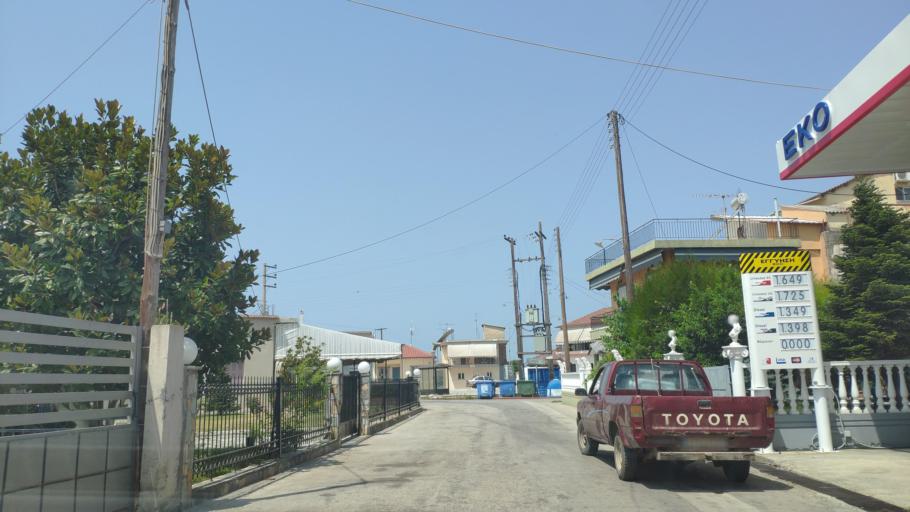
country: GR
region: Epirus
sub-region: Nomos Artas
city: Neochori
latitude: 39.0625
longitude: 21.0543
